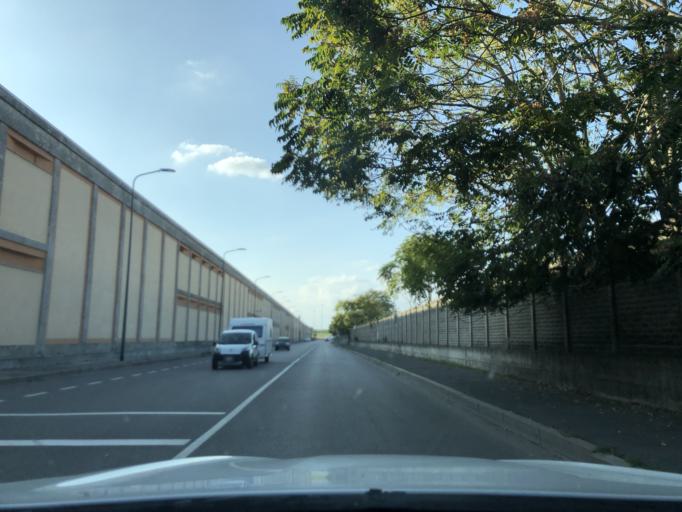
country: IT
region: Lombardy
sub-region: Citta metropolitana di Milano
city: Baranzate
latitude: 45.5085
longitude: 9.1181
